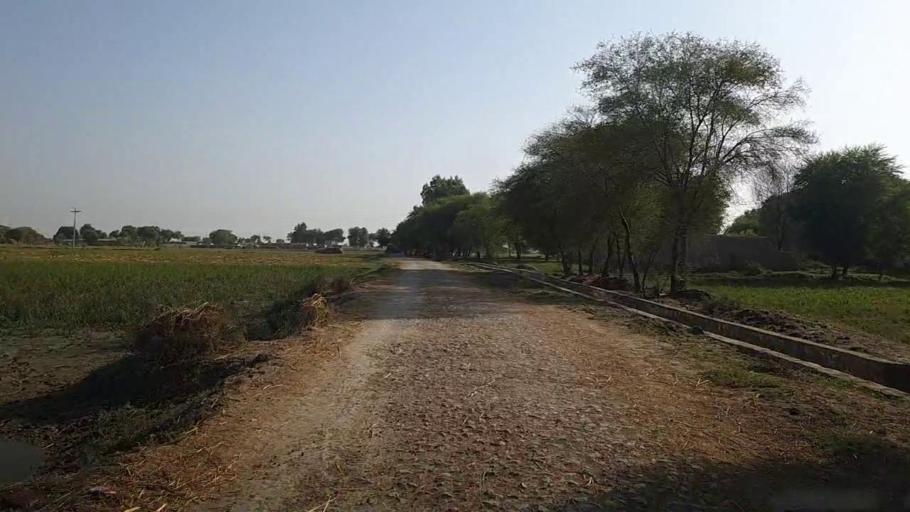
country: PK
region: Sindh
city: Kandhkot
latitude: 28.3542
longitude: 69.3350
